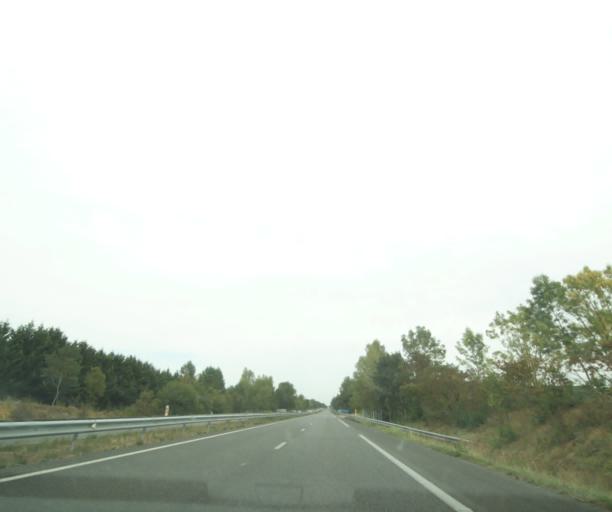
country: FR
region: Midi-Pyrenees
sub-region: Departement du Tarn-et-Garonne
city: Lamagistere
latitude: 44.1063
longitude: 0.7526
